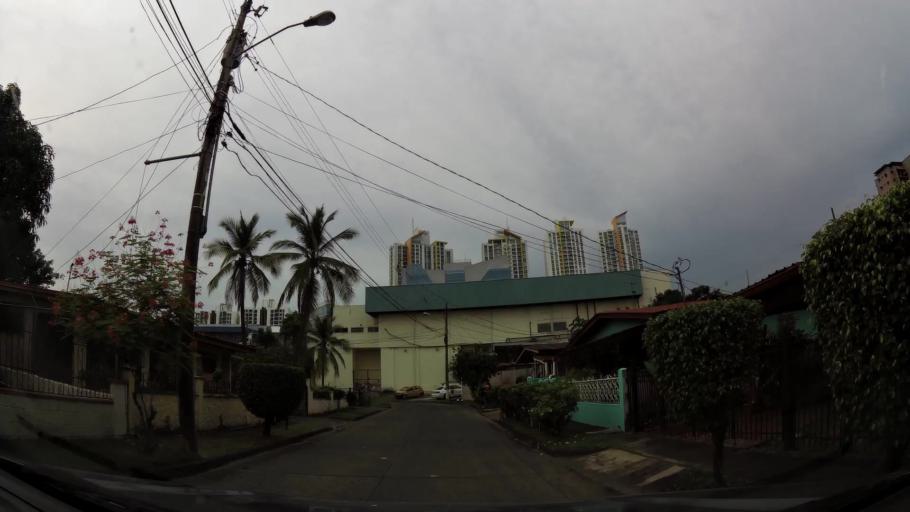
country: PA
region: Panama
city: Panama
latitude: 9.0244
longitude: -79.5220
